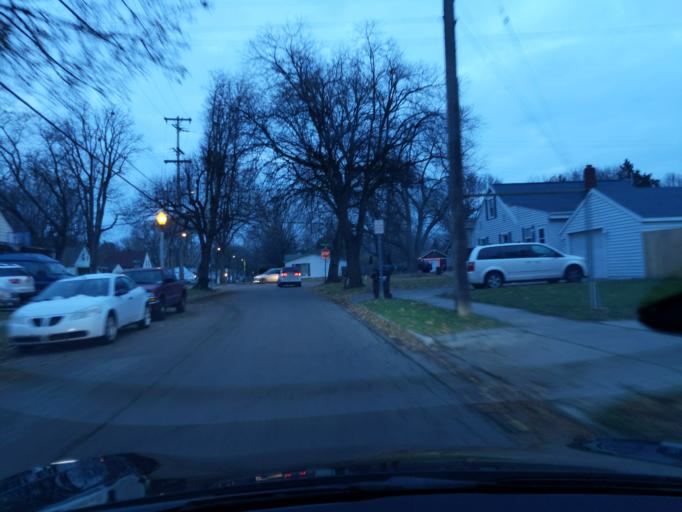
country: US
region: Michigan
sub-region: Ingham County
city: Lansing
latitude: 42.6969
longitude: -84.5584
